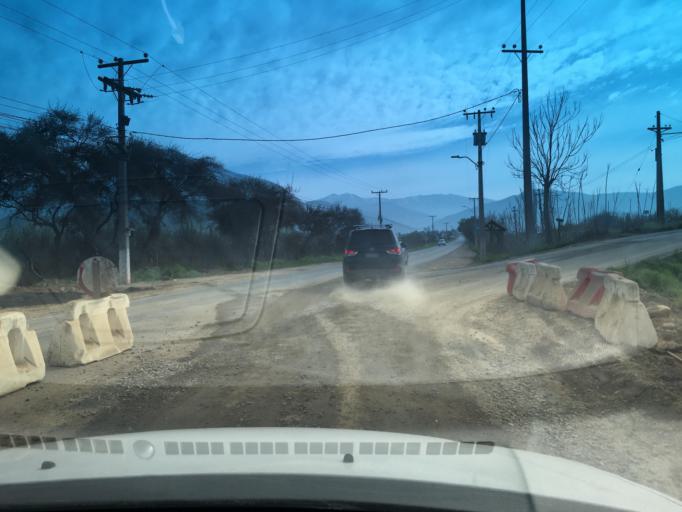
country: CL
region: Santiago Metropolitan
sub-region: Provincia de Chacabuco
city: Lampa
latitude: -33.1028
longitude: -70.9299
